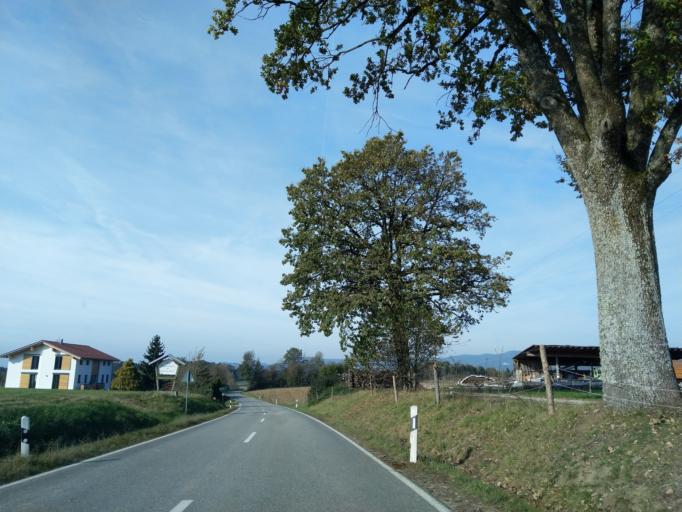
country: DE
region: Bavaria
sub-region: Lower Bavaria
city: Grattersdorf
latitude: 48.8071
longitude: 13.1464
